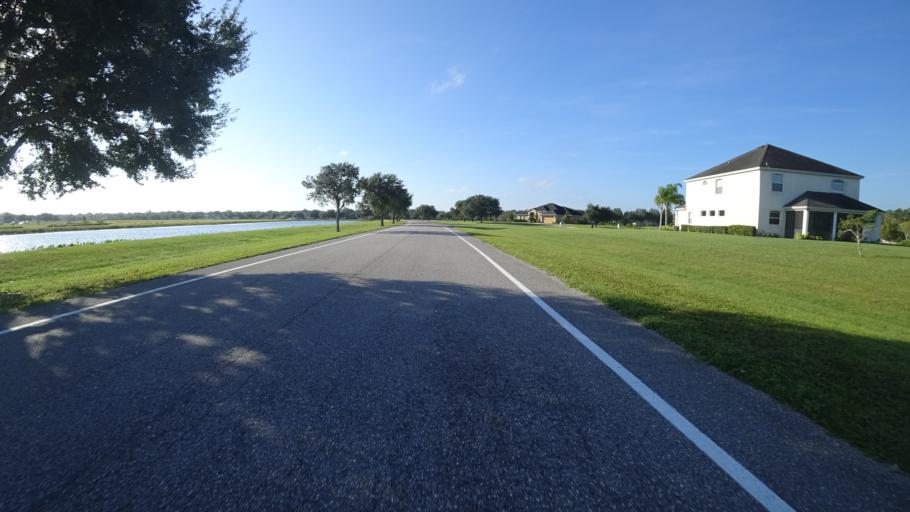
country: US
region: Florida
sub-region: Hillsborough County
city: Sun City Center
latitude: 27.5655
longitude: -82.3564
